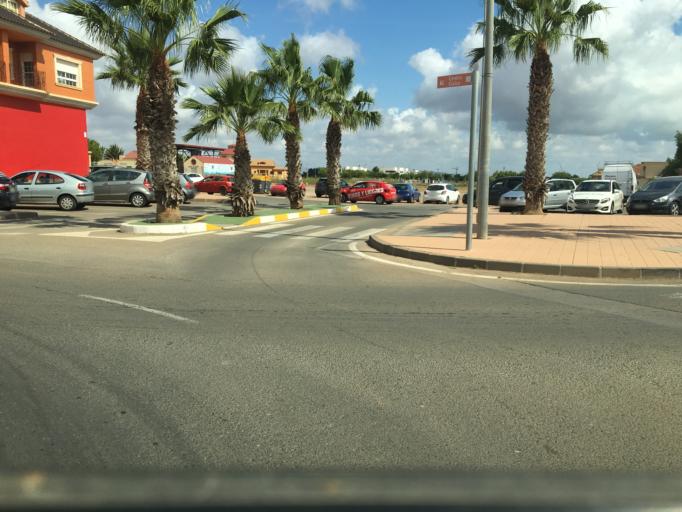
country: ES
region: Murcia
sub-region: Murcia
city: La Union
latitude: 37.6487
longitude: -0.8678
